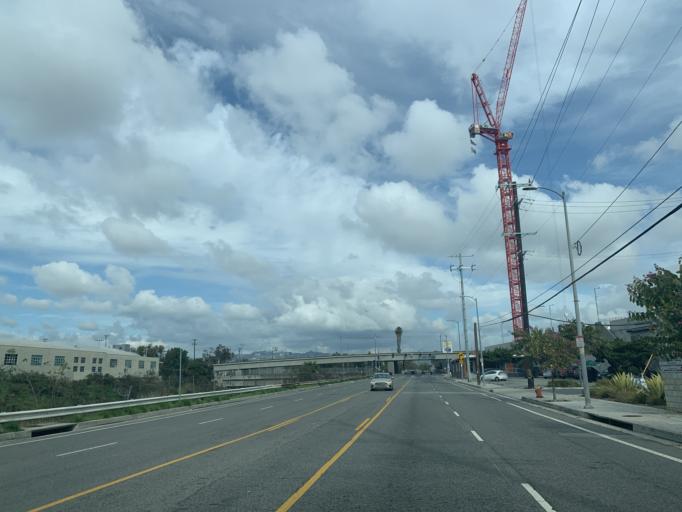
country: US
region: California
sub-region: Los Angeles County
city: Culver City
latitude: 34.0248
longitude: -118.3766
